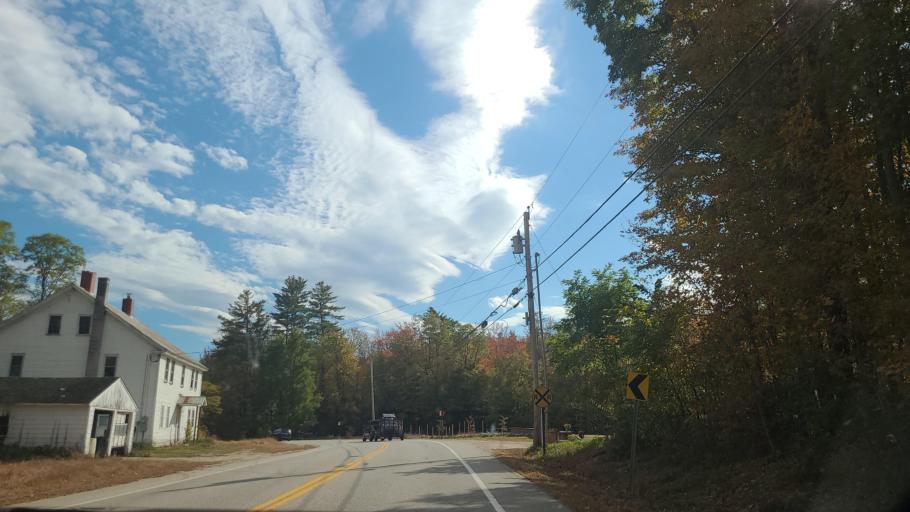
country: US
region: New Hampshire
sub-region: Carroll County
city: Conway
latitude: 44.0086
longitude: -71.1326
